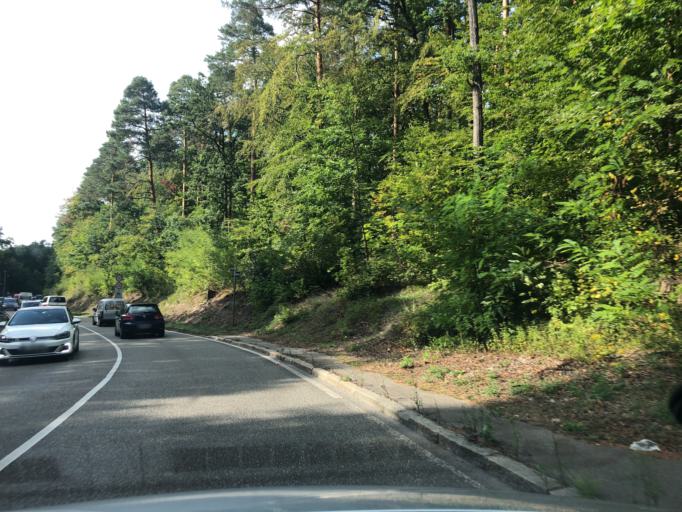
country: DE
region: Baden-Wuerttemberg
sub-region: Regierungsbezirk Stuttgart
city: Stuttgart
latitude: 48.7529
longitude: 9.1525
